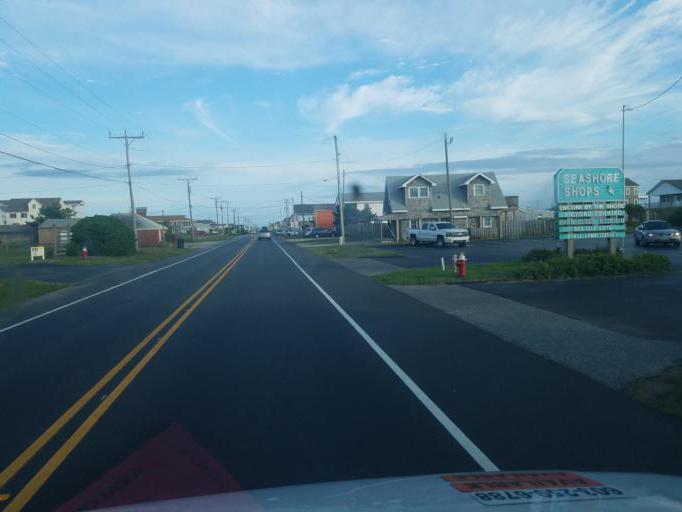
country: US
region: North Carolina
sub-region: Dare County
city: Kill Devil Hills
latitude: 36.0047
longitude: -75.6518
